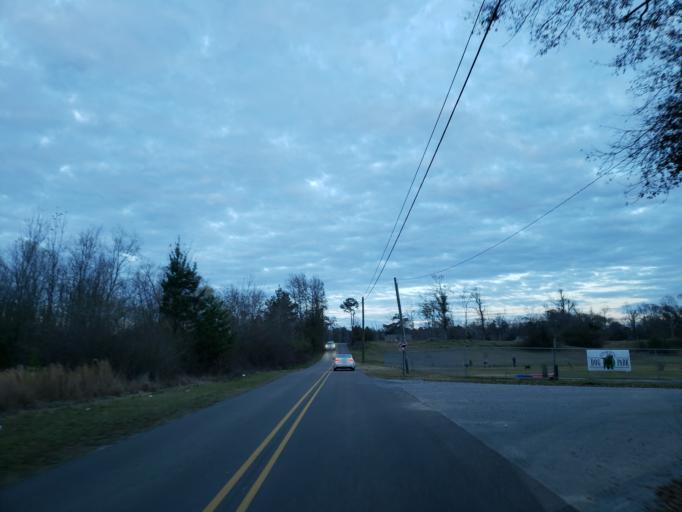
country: US
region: Mississippi
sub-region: Forrest County
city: Petal
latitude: 31.3292
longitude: -89.2629
